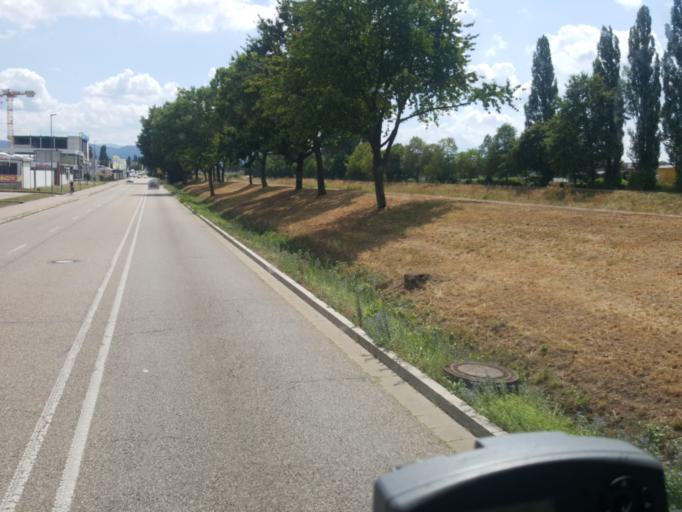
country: DE
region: Baden-Wuerttemberg
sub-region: Freiburg Region
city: Emmendingen
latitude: 48.1139
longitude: 7.8499
